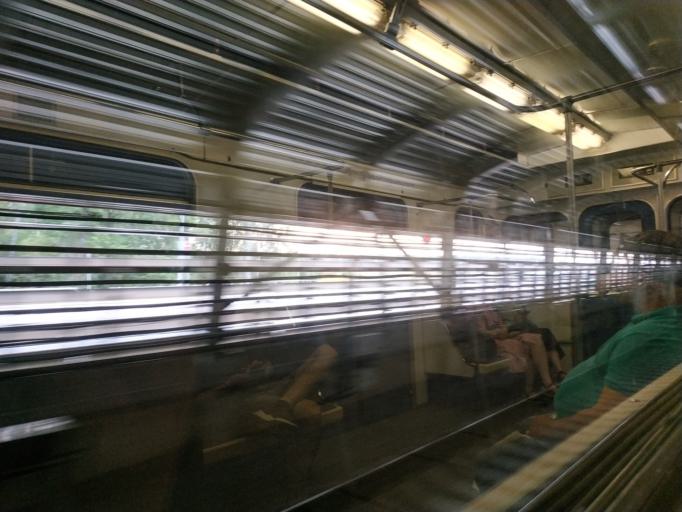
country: RU
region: Moskovskaya
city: Mosrentgen
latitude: 55.5817
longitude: 37.4446
